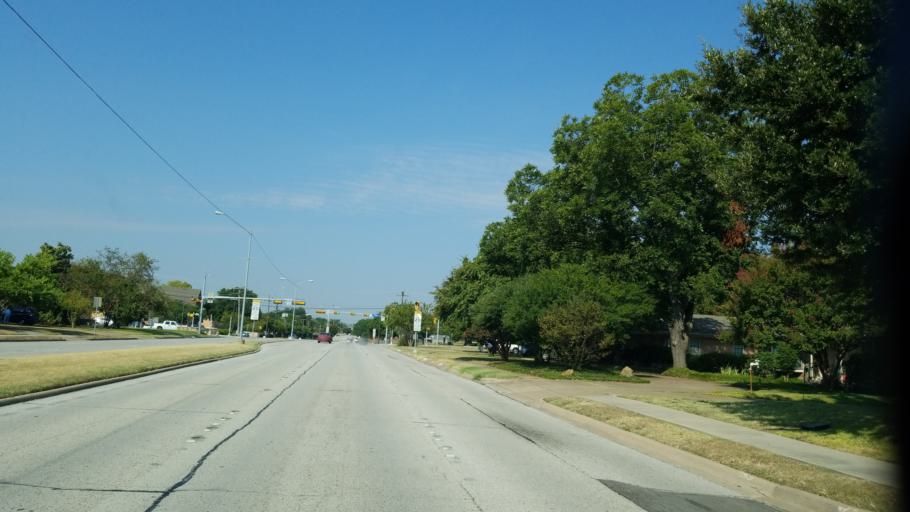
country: US
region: Texas
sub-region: Dallas County
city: Richardson
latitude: 32.9510
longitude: -96.7425
